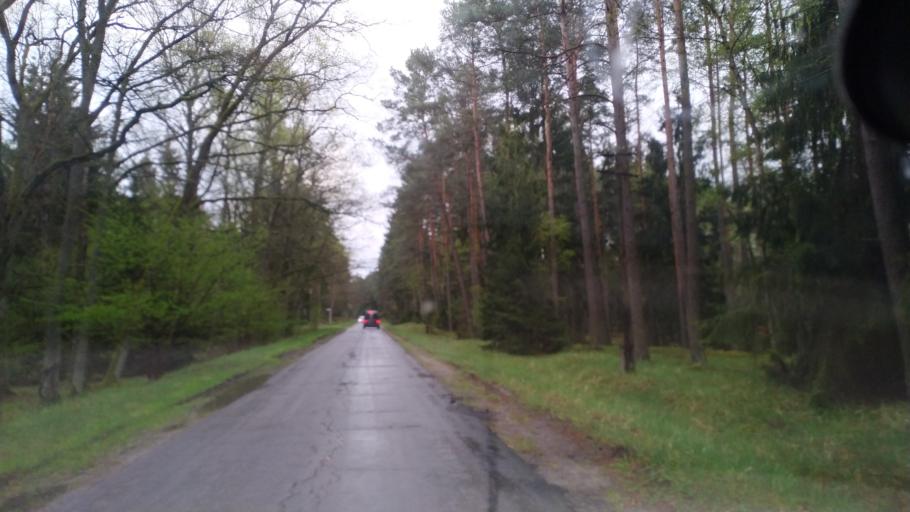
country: PL
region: Pomeranian Voivodeship
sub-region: Powiat starogardzki
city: Osiek
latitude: 53.6591
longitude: 18.4855
